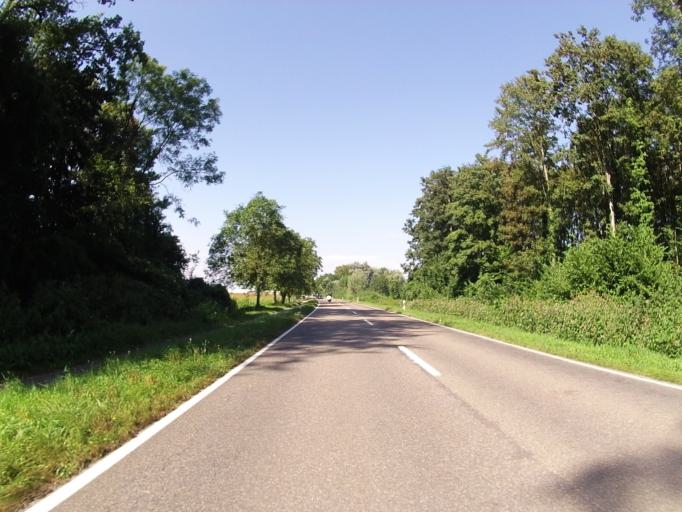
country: DE
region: Rheinland-Pfalz
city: Neuburg
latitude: 48.9993
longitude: 8.2598
